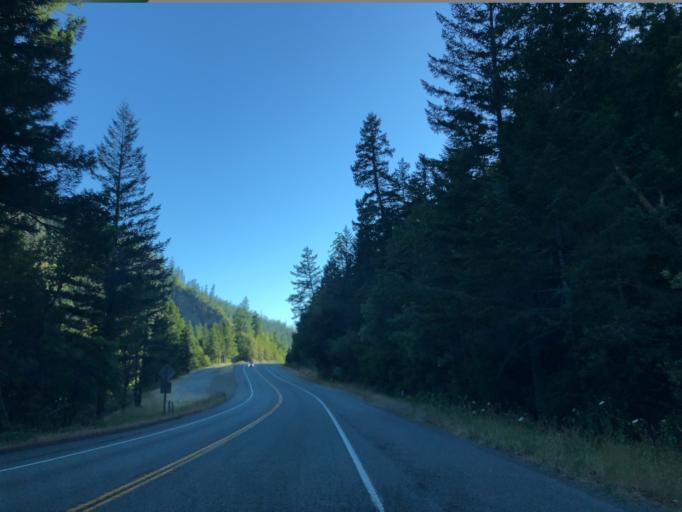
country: US
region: California
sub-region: Del Norte County
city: Bertsch-Oceanview
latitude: 41.8632
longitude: -123.8662
